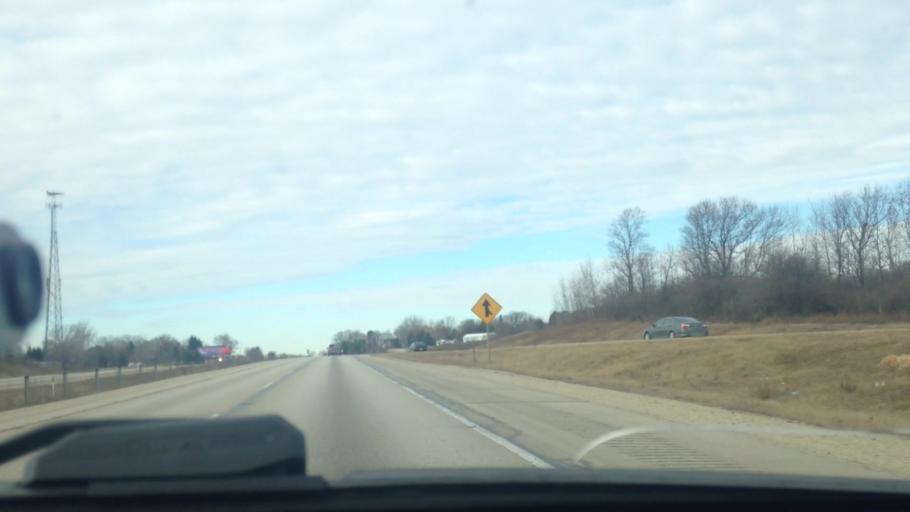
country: US
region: Wisconsin
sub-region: Washington County
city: Richfield
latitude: 43.2837
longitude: -88.1959
